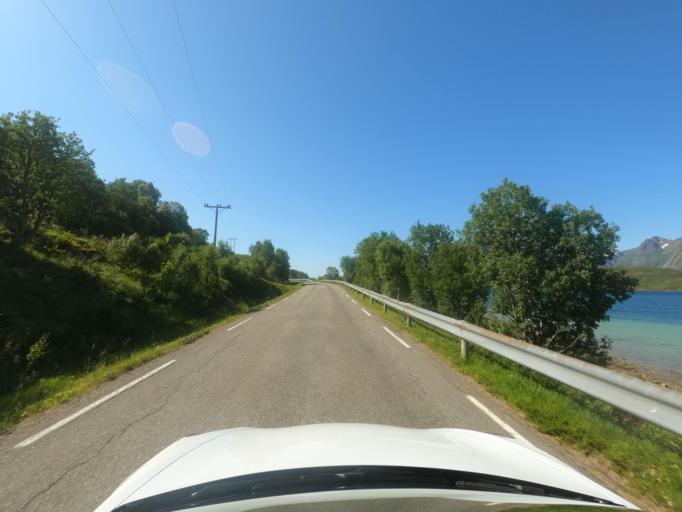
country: NO
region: Nordland
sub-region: Hadsel
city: Stokmarknes
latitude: 68.3609
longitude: 15.0680
